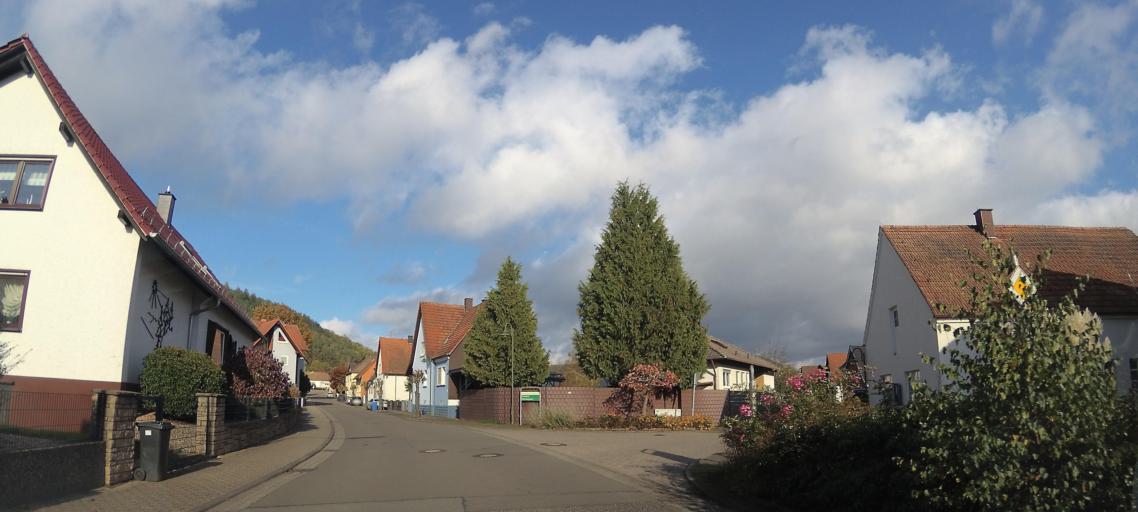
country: DE
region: Rheinland-Pfalz
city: Ruppertsweiler
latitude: 49.1962
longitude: 7.6846
